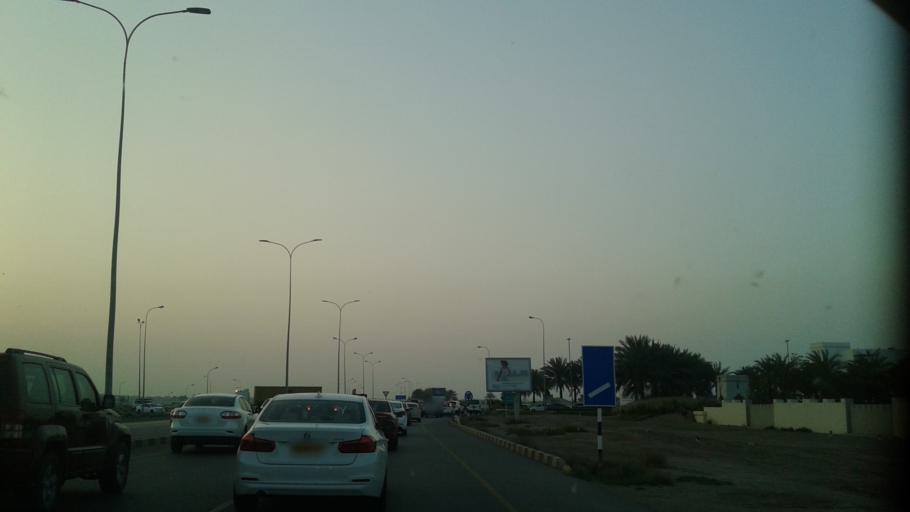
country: OM
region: Muhafazat Masqat
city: As Sib al Jadidah
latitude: 23.6246
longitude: 58.2652
